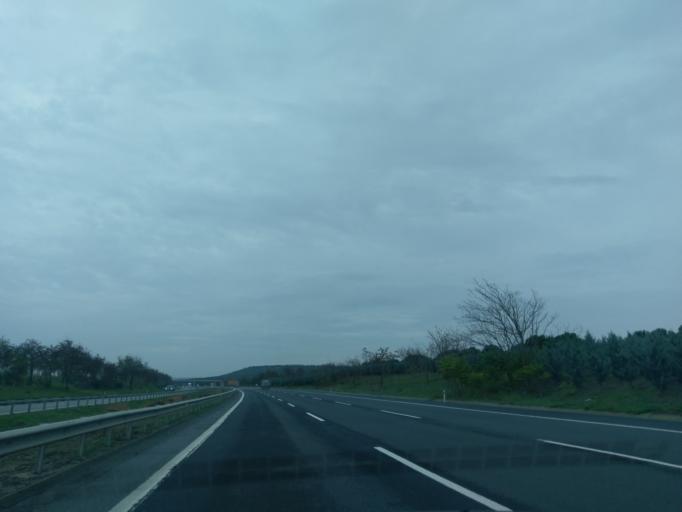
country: TR
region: Istanbul
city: Canta
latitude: 41.1561
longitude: 28.1413
